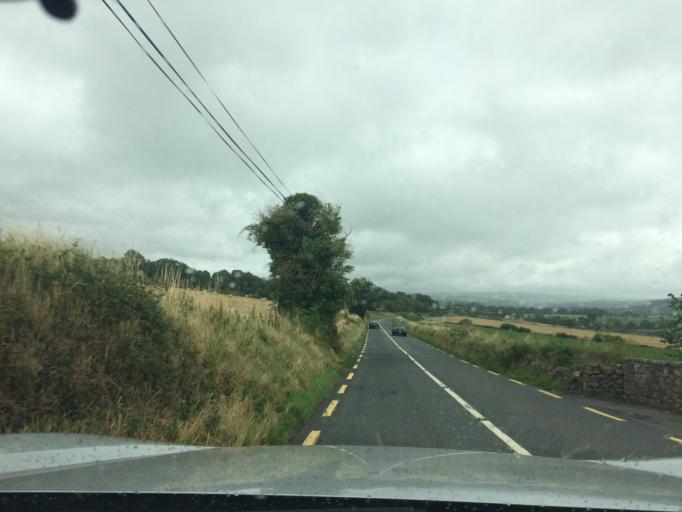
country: IE
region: Munster
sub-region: South Tipperary
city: Cluain Meala
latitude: 52.2948
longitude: -7.7818
